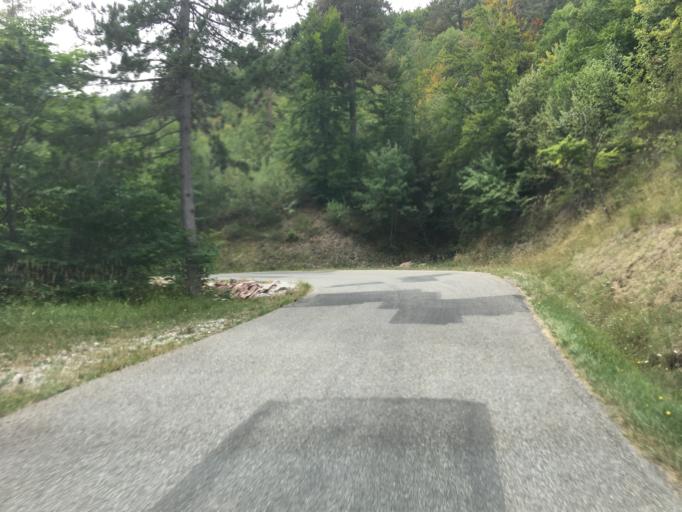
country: FR
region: Provence-Alpes-Cote d'Azur
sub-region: Departement des Alpes-de-Haute-Provence
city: Digne-les-Bains
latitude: 44.2176
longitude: 6.1421
